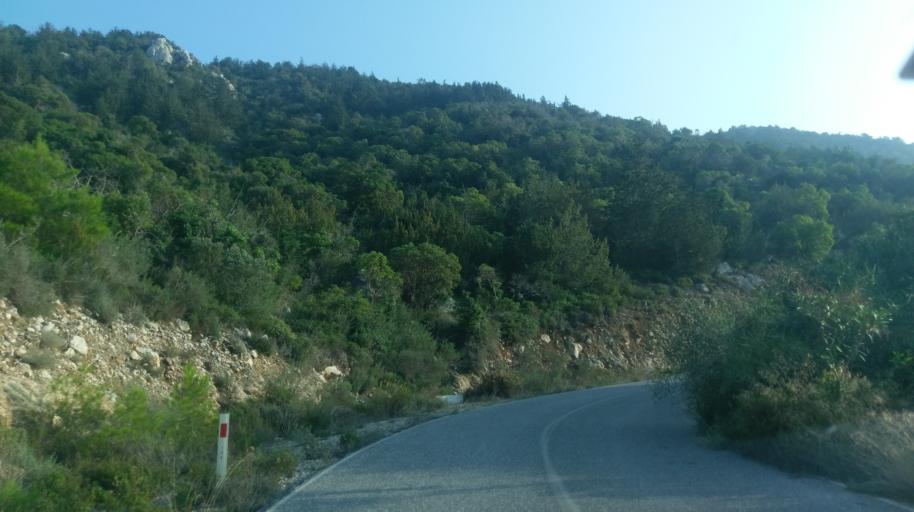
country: CY
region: Ammochostos
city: Trikomo
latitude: 35.4025
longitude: 33.9043
